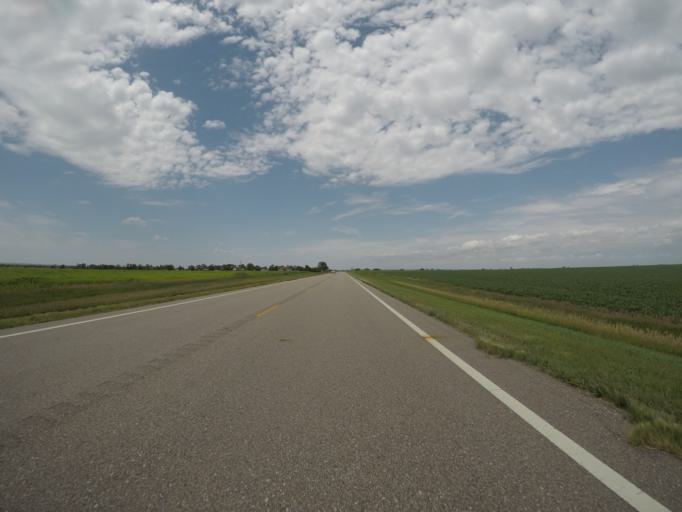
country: US
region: Kansas
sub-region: Graham County
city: Hill City
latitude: 39.3945
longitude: -99.6084
